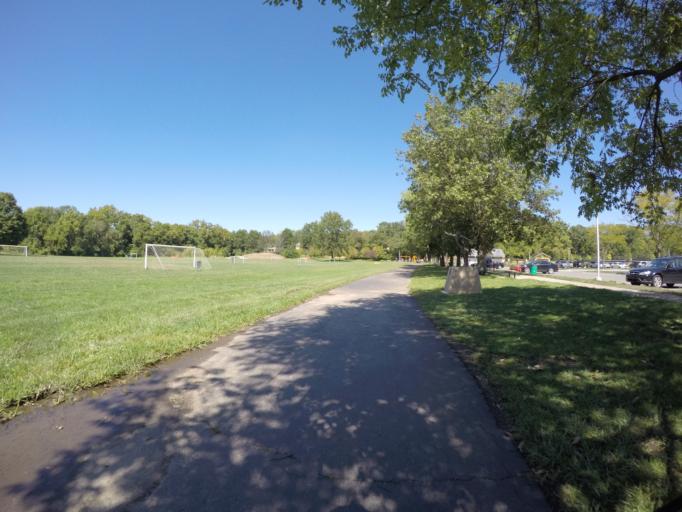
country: US
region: Kansas
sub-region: Johnson County
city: Leawood
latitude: 38.9397
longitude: -94.6414
